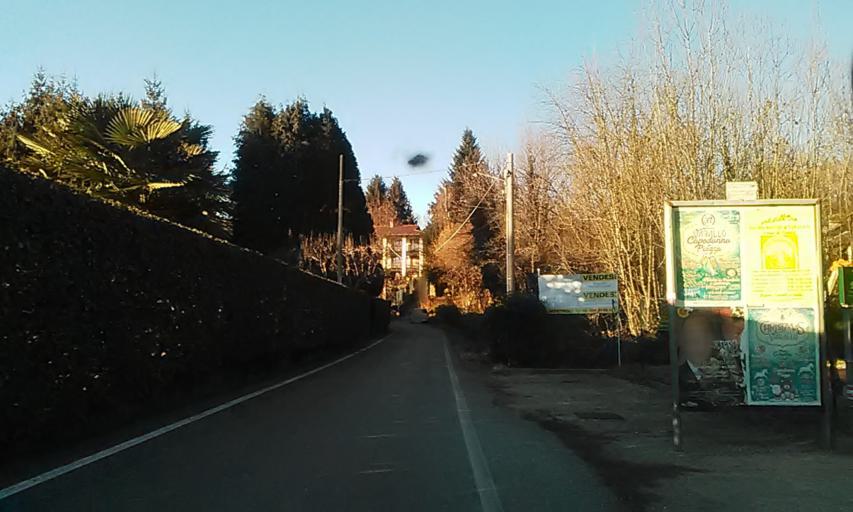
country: IT
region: Piedmont
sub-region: Provincia di Vercelli
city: Borgosesia
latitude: 45.7313
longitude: 8.2678
